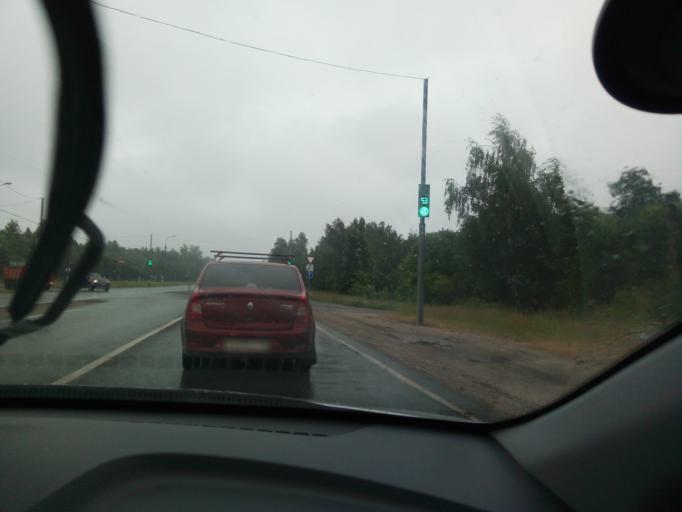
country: RU
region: Chuvashia
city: Novyye Lapsary
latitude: 56.0805
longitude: 47.1362
